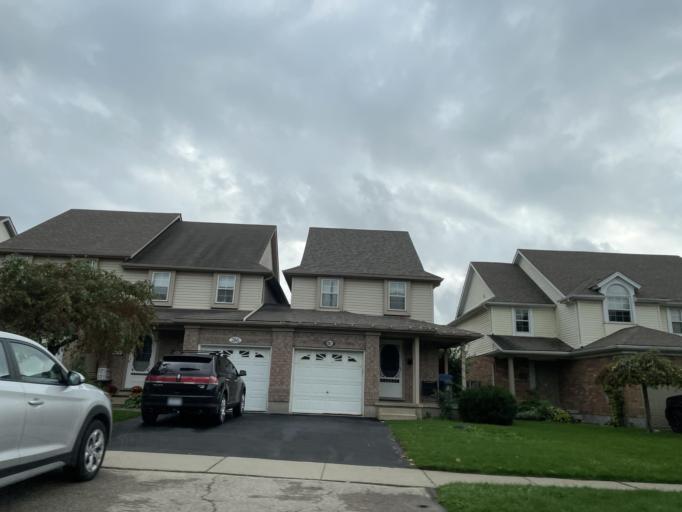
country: CA
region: Ontario
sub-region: Wellington County
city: Guelph
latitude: 43.5670
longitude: -80.2250
